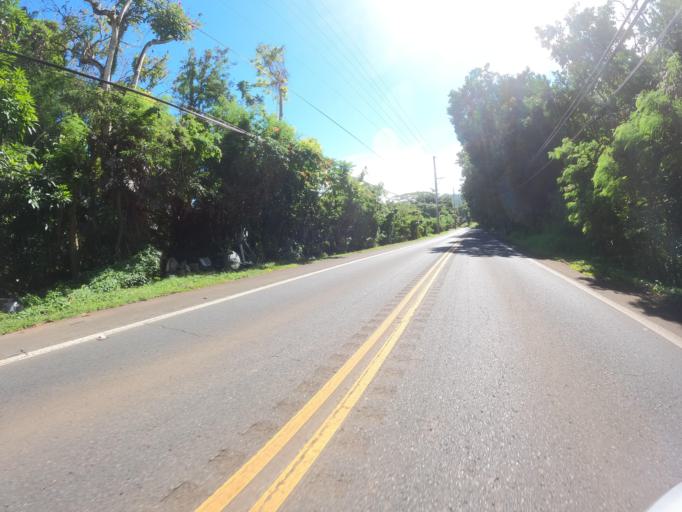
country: US
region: Hawaii
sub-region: Honolulu County
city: Kahalu'u
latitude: 21.4930
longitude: -157.8507
